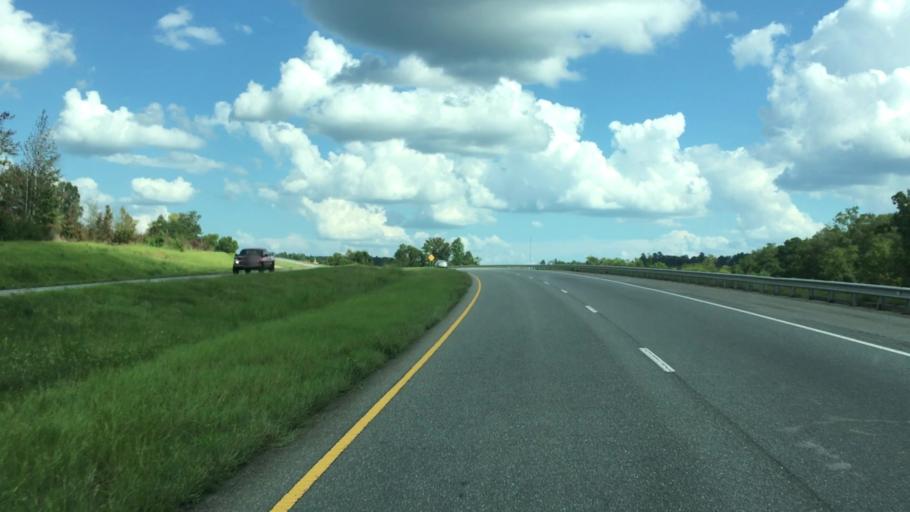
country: US
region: Georgia
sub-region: Wilkinson County
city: Irwinton
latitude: 32.6969
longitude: -83.1169
